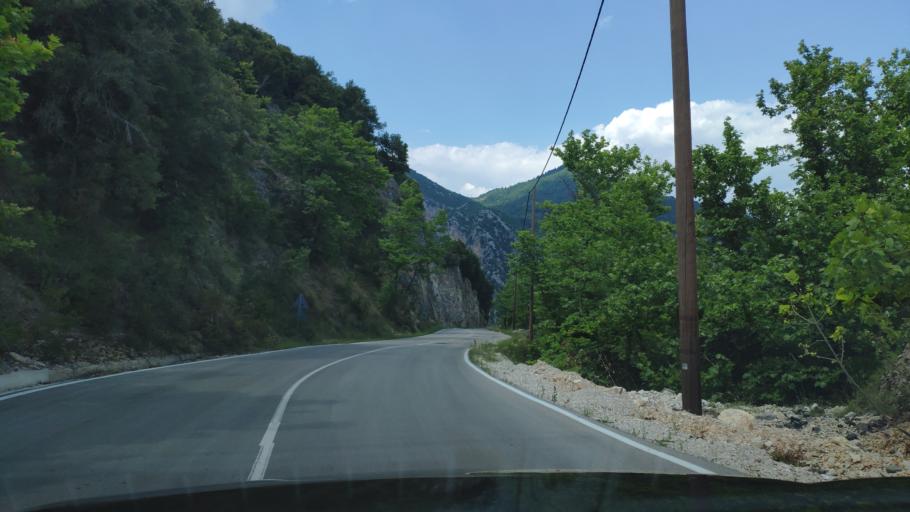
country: GR
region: Epirus
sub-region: Nomos Artas
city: Agios Dimitrios
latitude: 39.4611
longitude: 21.0230
